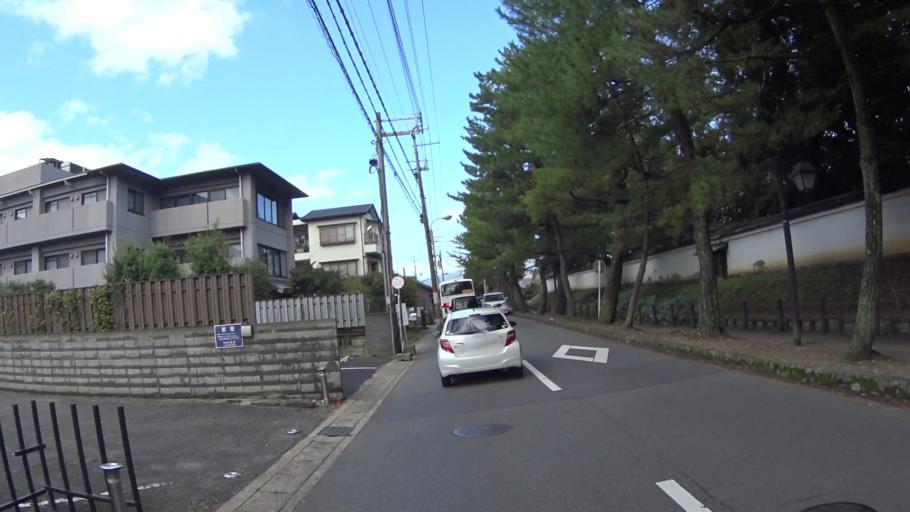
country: JP
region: Kyoto
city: Uji
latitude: 34.9522
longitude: 135.8179
